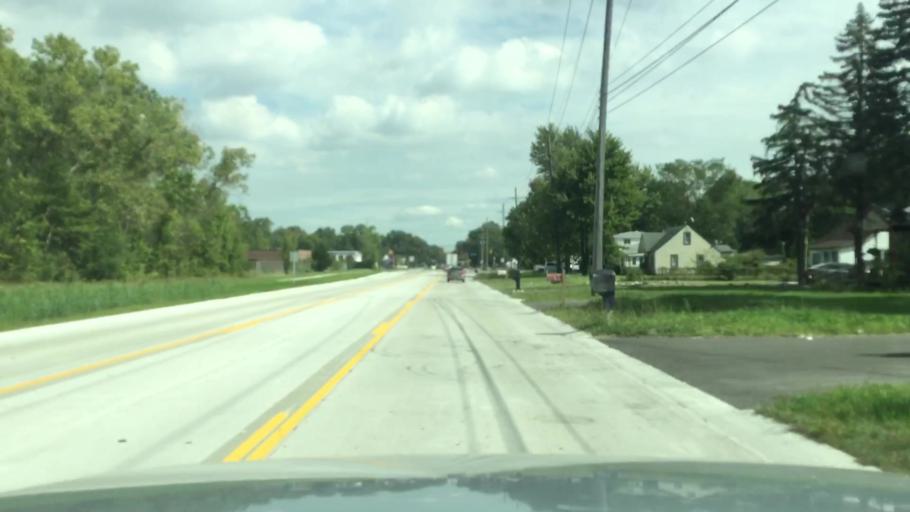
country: US
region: Michigan
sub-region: Wayne County
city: Wayne
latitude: 42.2528
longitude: -83.3519
